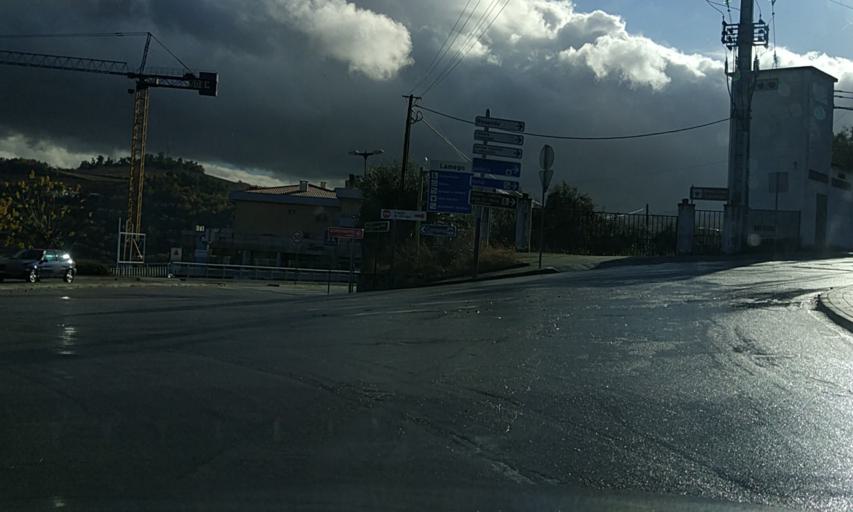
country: PT
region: Viseu
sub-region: Lamego
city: Lamego
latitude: 41.1045
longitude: -7.7949
